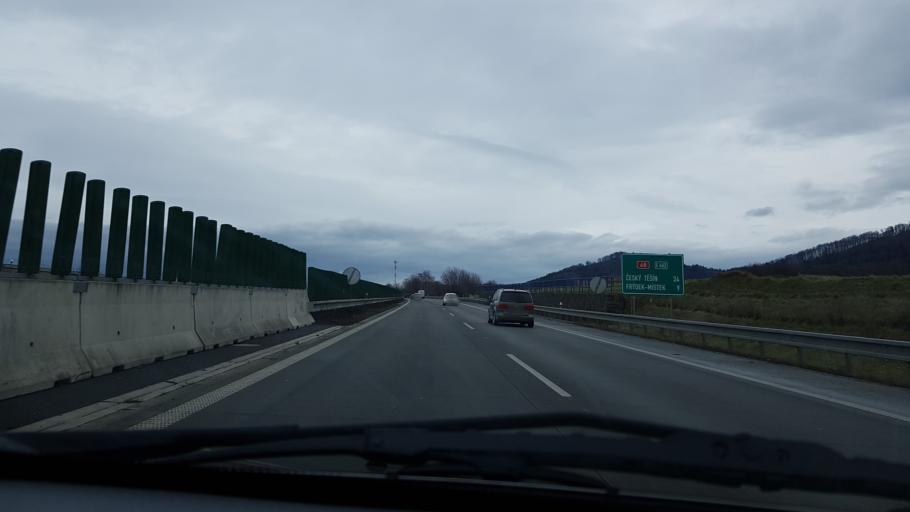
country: CZ
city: Frycovice
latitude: 49.6504
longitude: 18.2253
